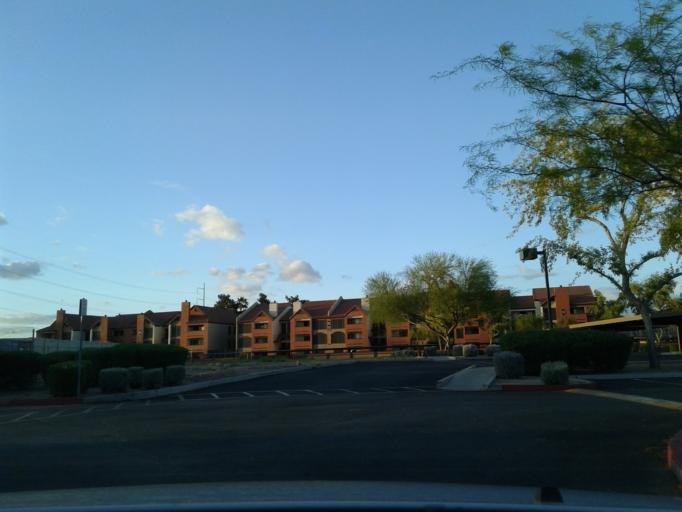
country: US
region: Arizona
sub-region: Maricopa County
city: Glendale
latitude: 33.5918
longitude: -112.1155
